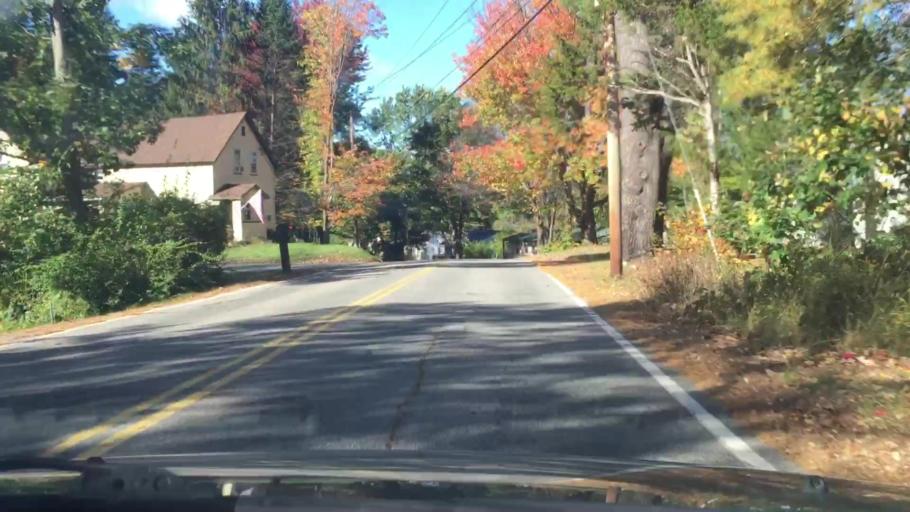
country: US
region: New Hampshire
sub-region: Cheshire County
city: Keene
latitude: 42.9073
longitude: -72.2887
